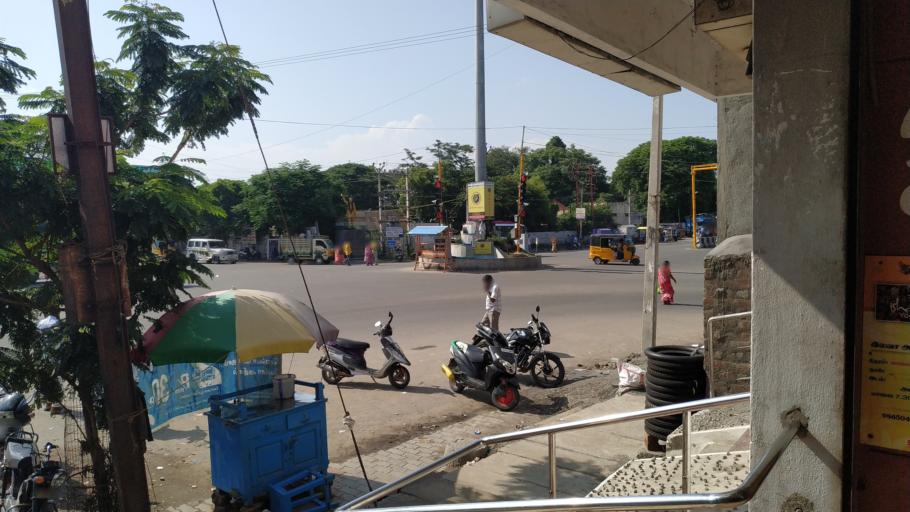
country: IN
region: Tamil Nadu
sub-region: Villupuram
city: Villupuram
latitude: 11.9399
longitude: 79.4862
